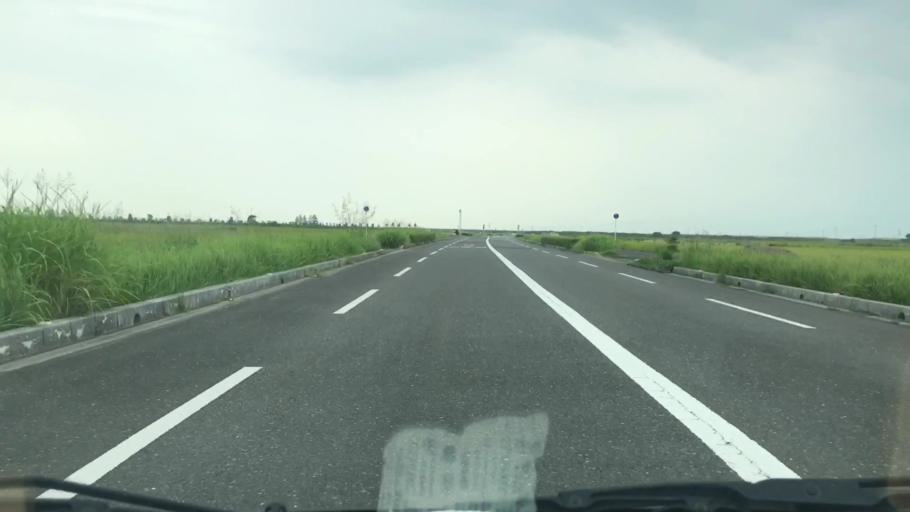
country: JP
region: Saga Prefecture
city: Okawa
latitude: 33.1678
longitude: 130.2933
